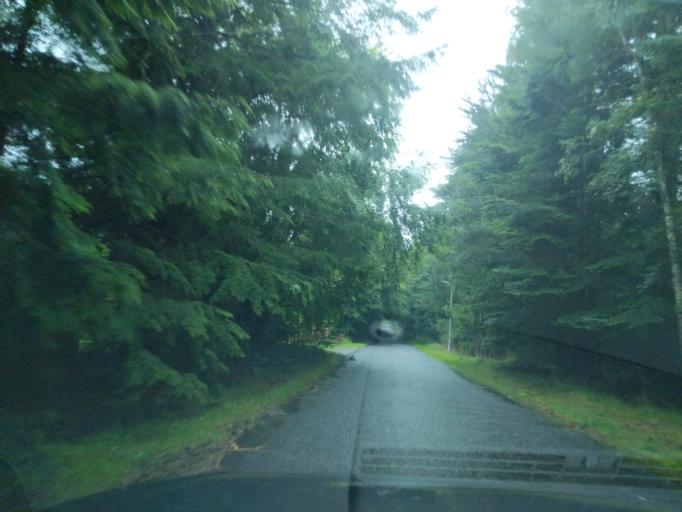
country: GB
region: Scotland
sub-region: Aberdeenshire
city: Aboyne
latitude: 57.0737
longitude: -2.8034
